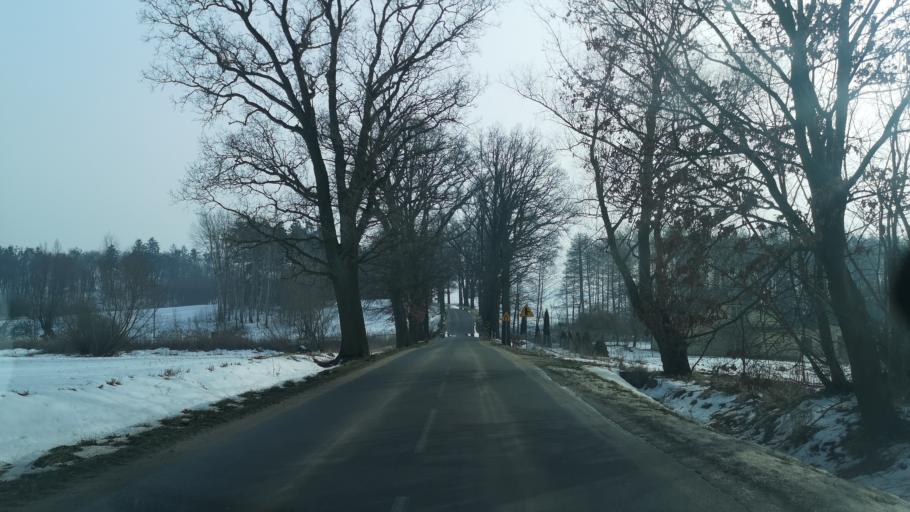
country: PL
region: Warmian-Masurian Voivodeship
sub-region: Powiat nowomiejski
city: Biskupiec
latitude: 53.5242
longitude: 19.3442
